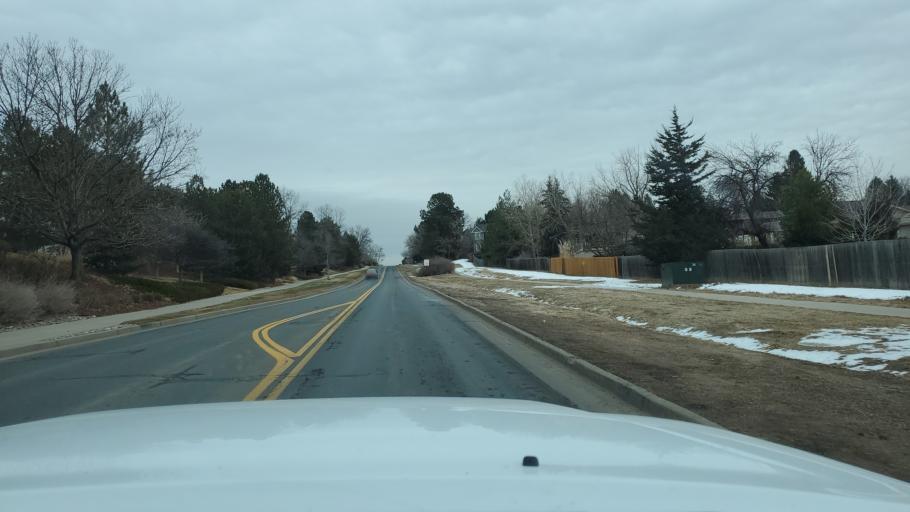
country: US
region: Colorado
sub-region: Arapahoe County
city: Greenwood Village
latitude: 39.6096
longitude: -104.9364
